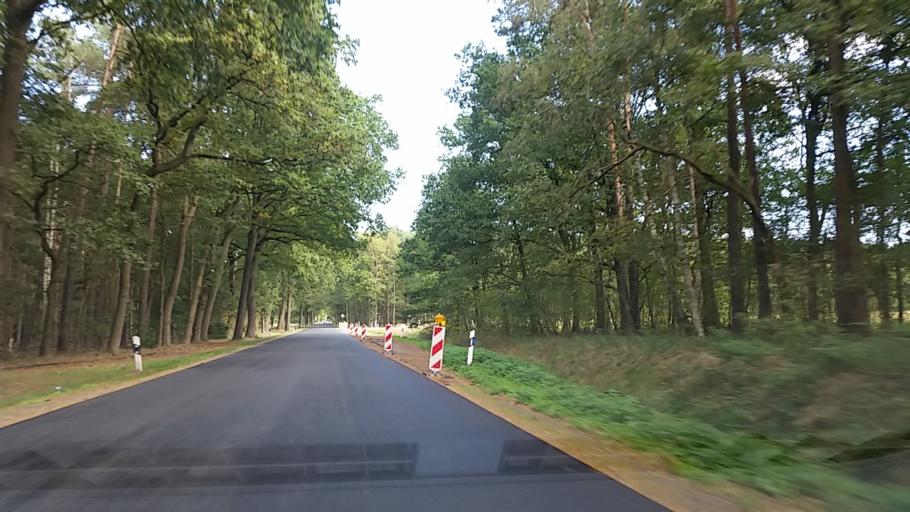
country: DE
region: Lower Saxony
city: Visselhovede
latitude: 53.0102
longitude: 9.6412
